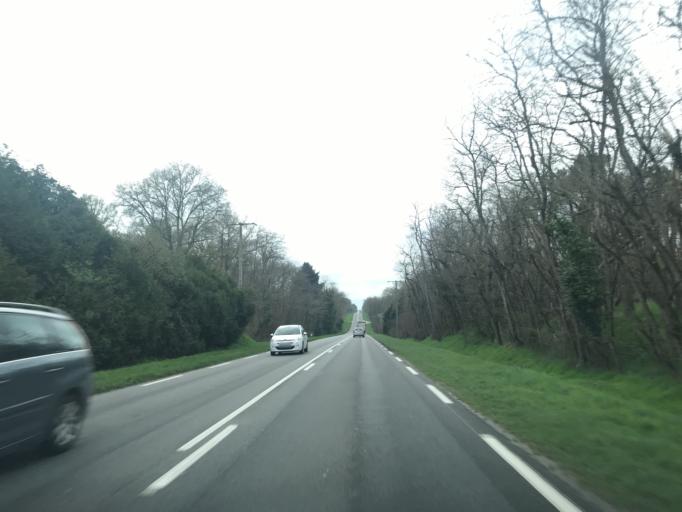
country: FR
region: Centre
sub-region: Departement du Loiret
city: Bray-en-Val
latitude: 47.8357
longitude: 2.3545
